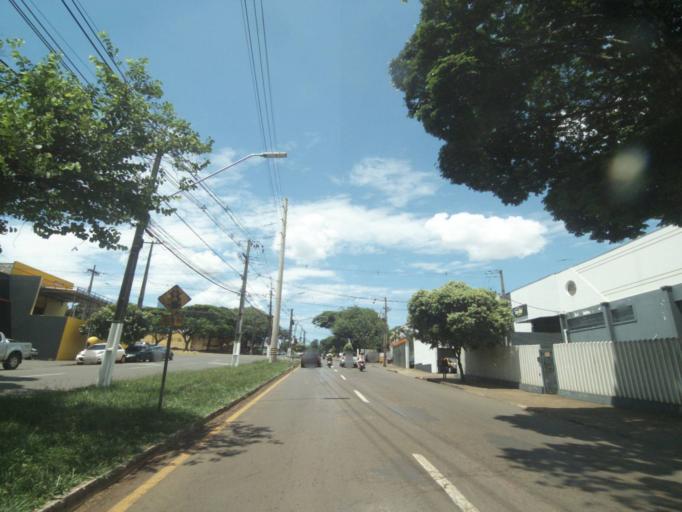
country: BR
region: Parana
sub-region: Londrina
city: Londrina
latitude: -23.3105
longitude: -51.2044
